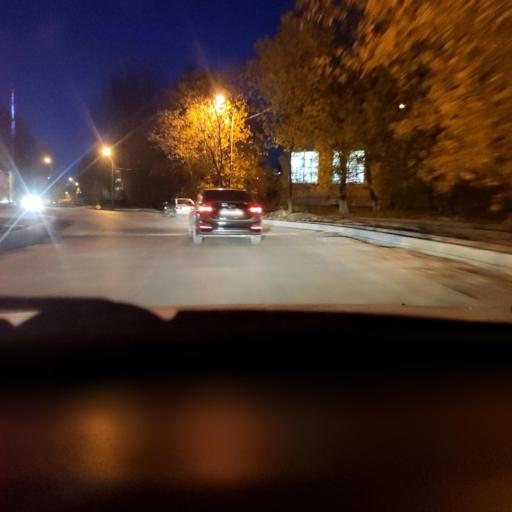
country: RU
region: Perm
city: Perm
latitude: 58.0096
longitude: 56.2647
